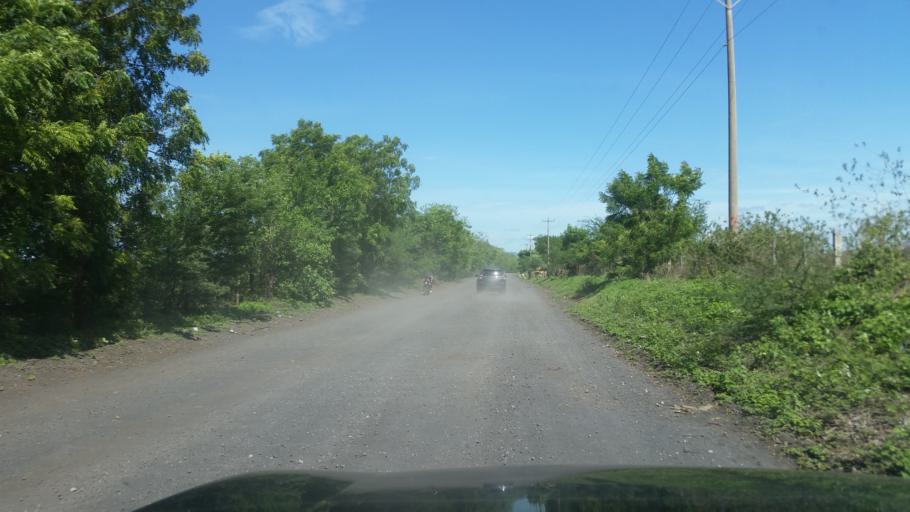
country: NI
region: Chinandega
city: Puerto Morazan
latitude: 12.7686
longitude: -87.0673
